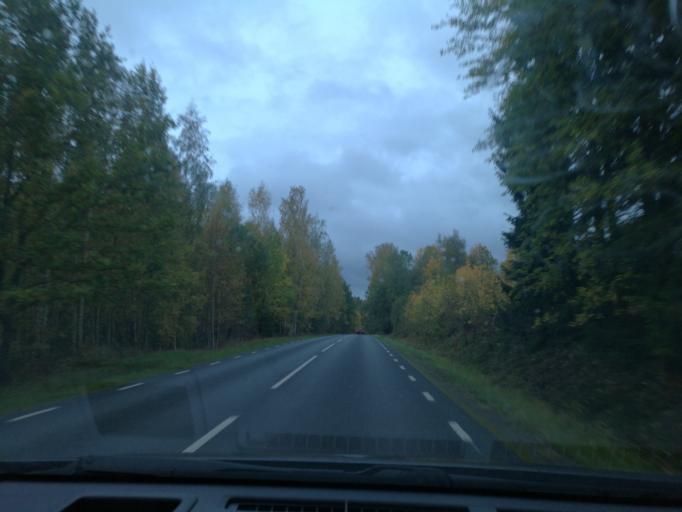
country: SE
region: Soedermanland
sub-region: Vingakers Kommun
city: Vingaker
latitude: 59.0708
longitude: 15.8915
